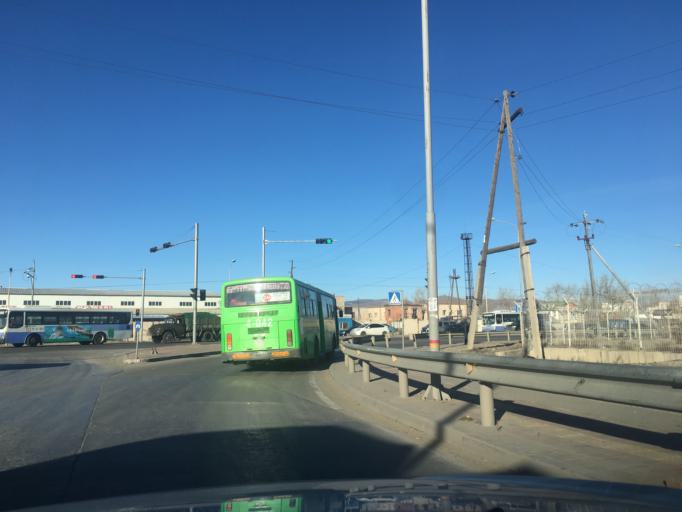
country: MN
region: Ulaanbaatar
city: Ulaanbaatar
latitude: 47.9068
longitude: 106.7861
